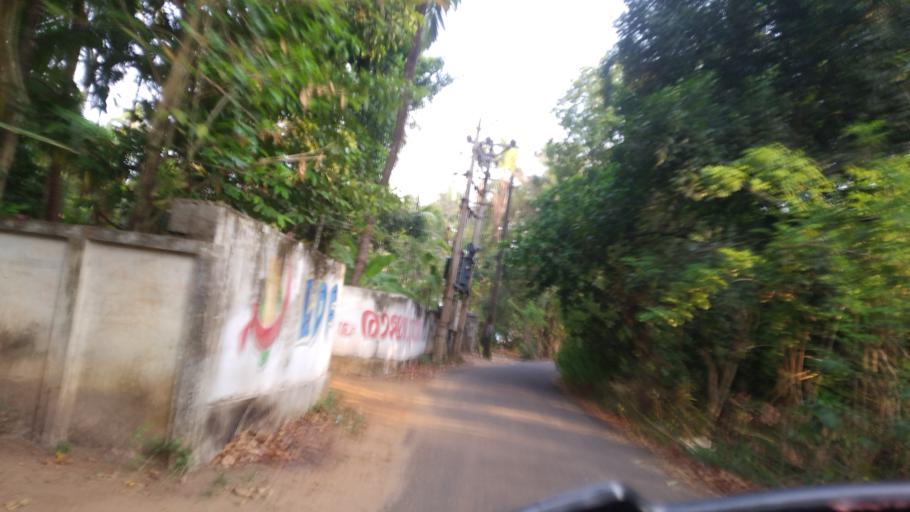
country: IN
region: Kerala
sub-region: Thrissur District
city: Thanniyam
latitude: 10.4121
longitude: 76.0883
